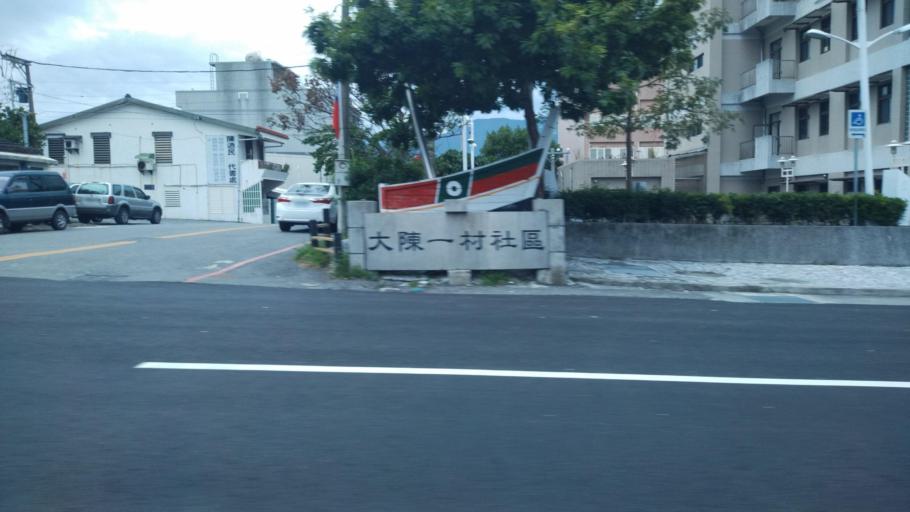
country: TW
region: Taiwan
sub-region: Hualien
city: Hualian
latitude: 24.0053
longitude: 121.6186
